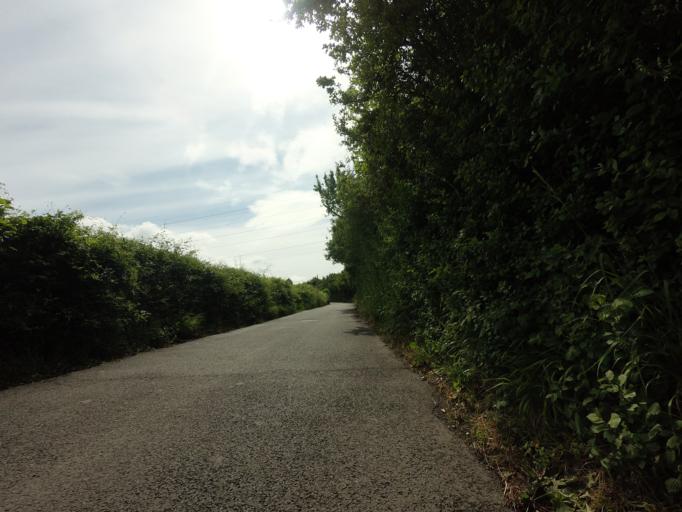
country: GB
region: England
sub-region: Kent
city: Halstead
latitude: 51.3555
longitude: 0.1345
